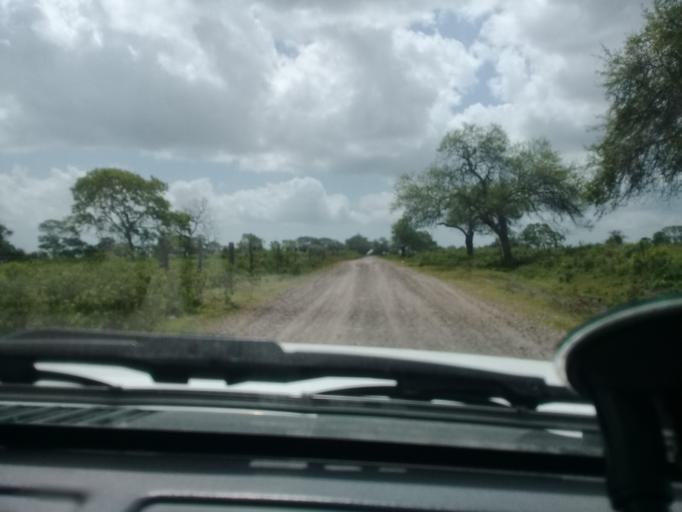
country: MX
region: Veracruz
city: Moralillo
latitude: 22.1597
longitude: -97.9941
